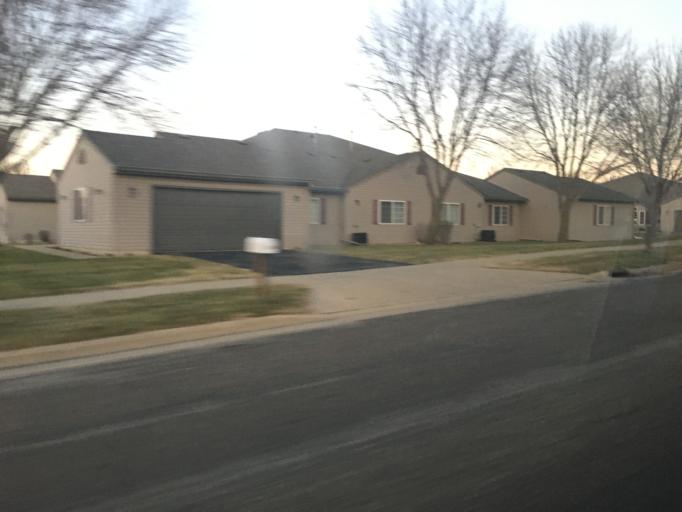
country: US
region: Minnesota
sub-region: Olmsted County
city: Rochester
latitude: 44.0727
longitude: -92.5118
